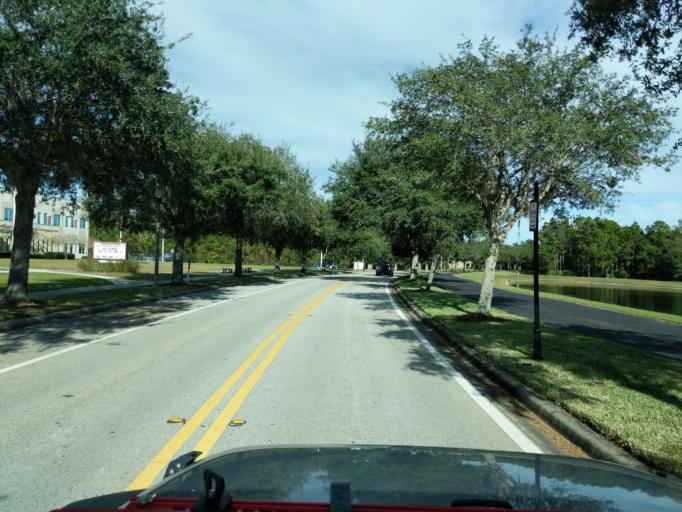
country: US
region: Florida
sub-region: Orange County
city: Lake Butler
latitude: 28.4664
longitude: -81.6063
